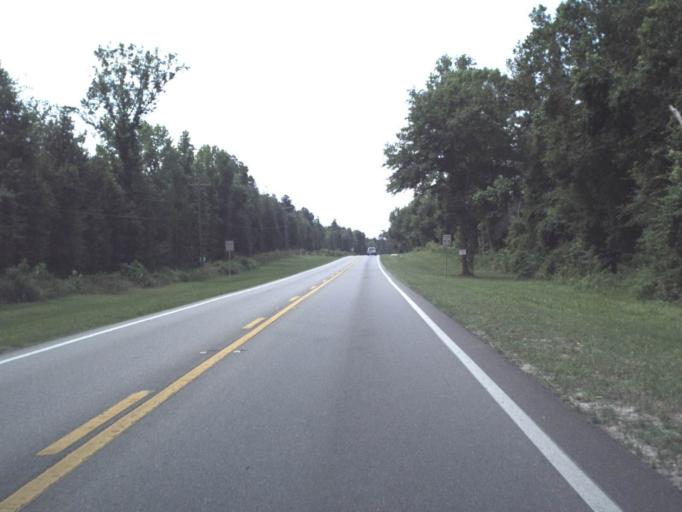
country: US
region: Florida
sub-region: Clay County
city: Keystone Heights
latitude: 29.7506
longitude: -82.0554
